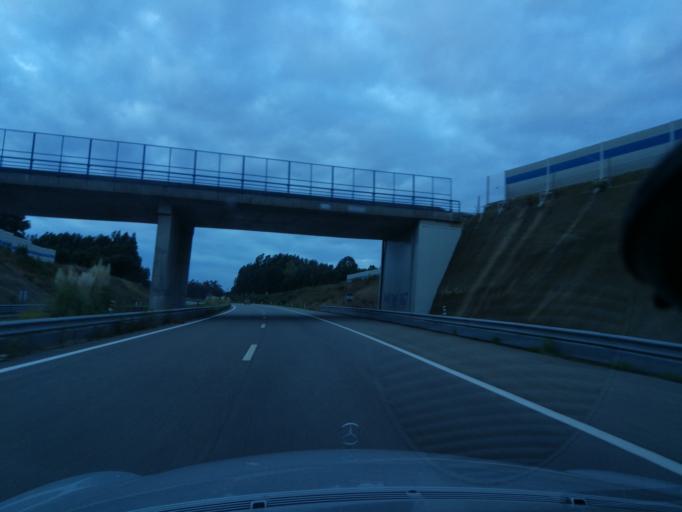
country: PT
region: Aveiro
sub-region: Estarreja
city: Beduido
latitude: 40.7683
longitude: -8.5549
